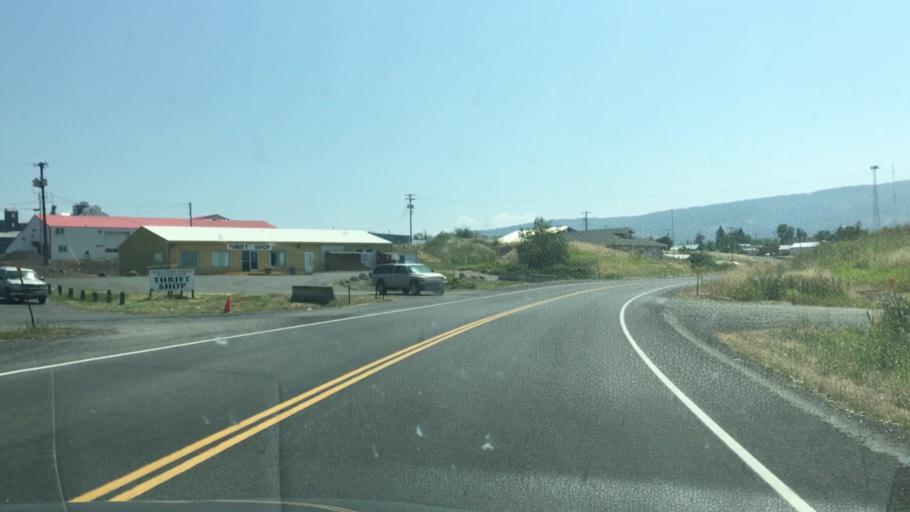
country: US
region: Idaho
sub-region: Idaho County
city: Grangeville
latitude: 45.9352
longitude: -116.1339
